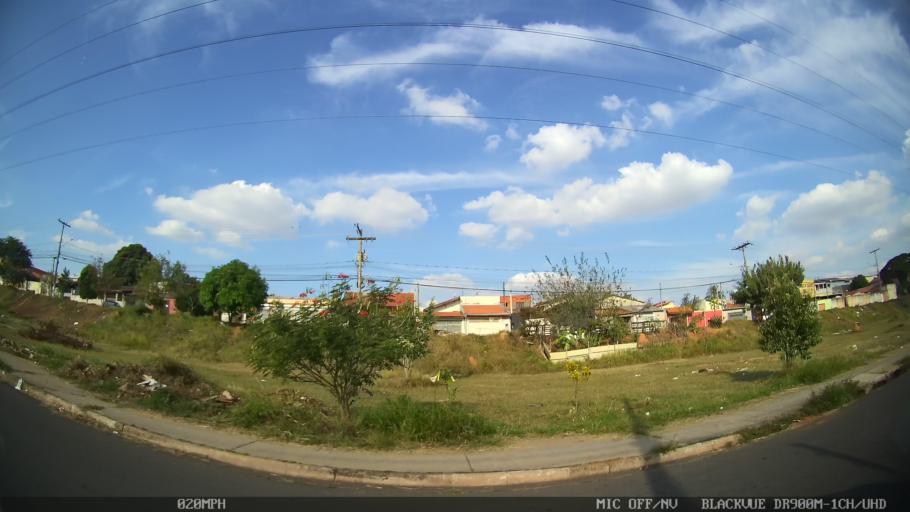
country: BR
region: Sao Paulo
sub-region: Hortolandia
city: Hortolandia
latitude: -22.8554
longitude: -47.1958
